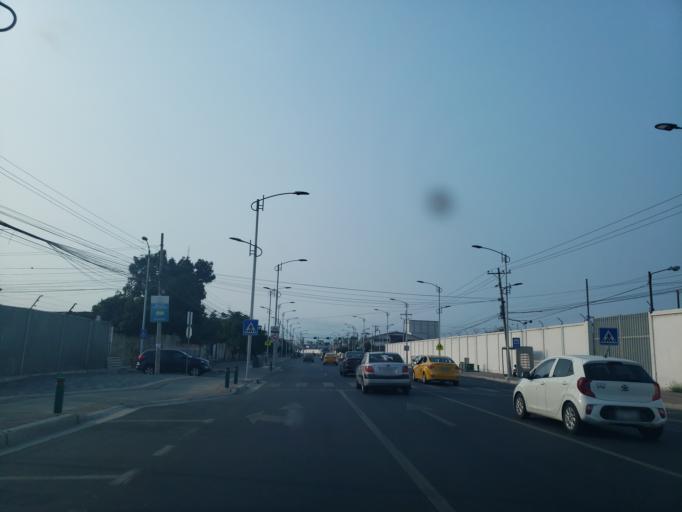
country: EC
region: Manabi
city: Manta
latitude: -0.9658
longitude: -80.7048
